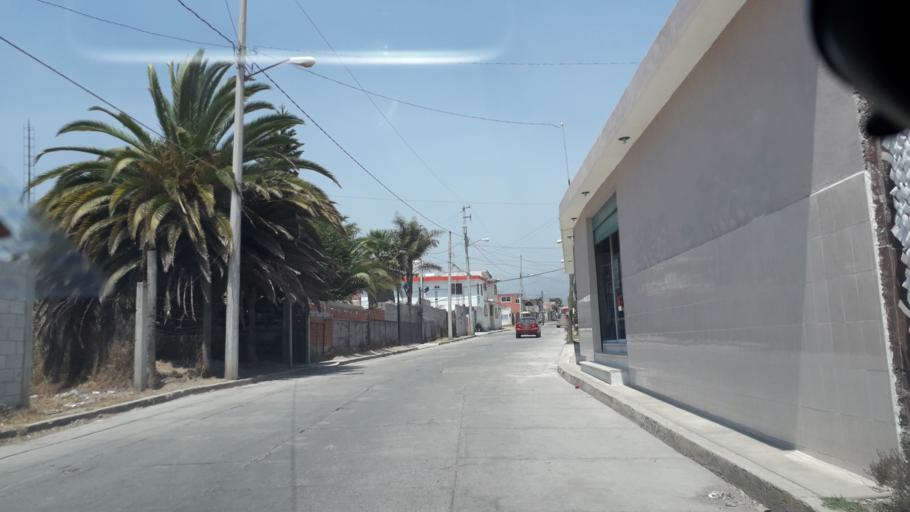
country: MX
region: Puebla
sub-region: Puebla
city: Santa Maria Xonacatepec
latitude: 19.0837
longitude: -98.1097
